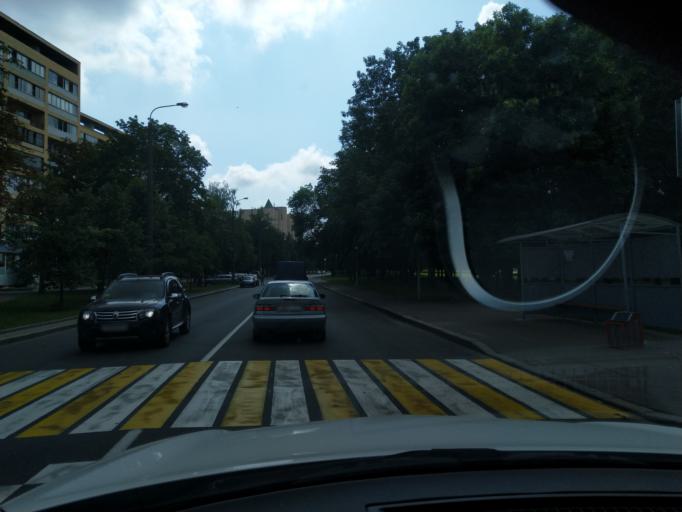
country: BY
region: Minsk
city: Minsk
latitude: 53.8966
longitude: 27.5803
